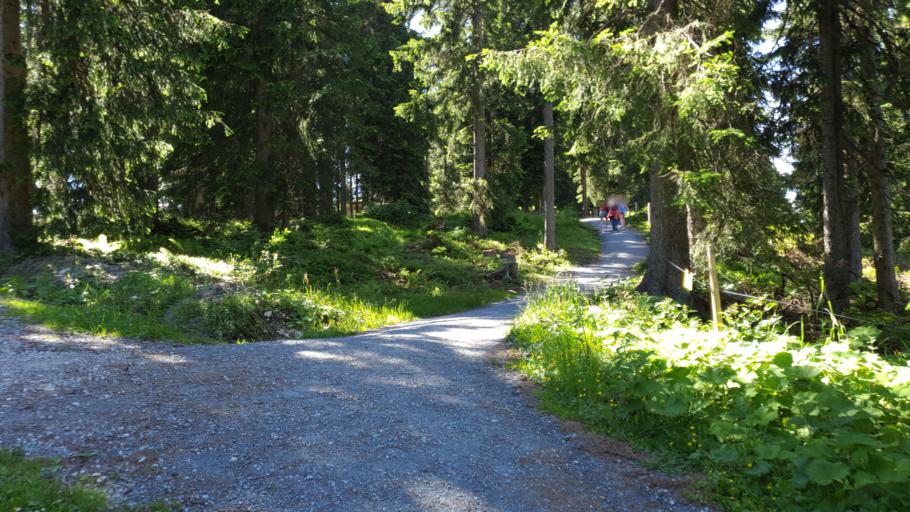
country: AT
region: Tyrol
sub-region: Politischer Bezirk Kufstein
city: Scheffau am Wilden Kaiser
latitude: 47.4901
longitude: 12.2508
